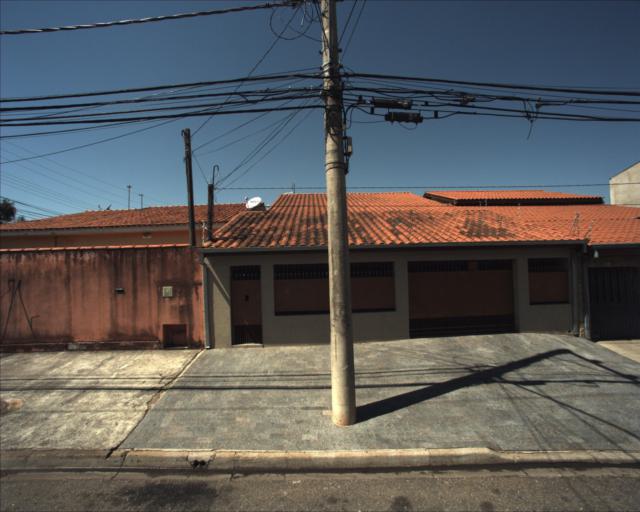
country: BR
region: Sao Paulo
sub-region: Sorocaba
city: Sorocaba
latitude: -23.4694
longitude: -47.4863
